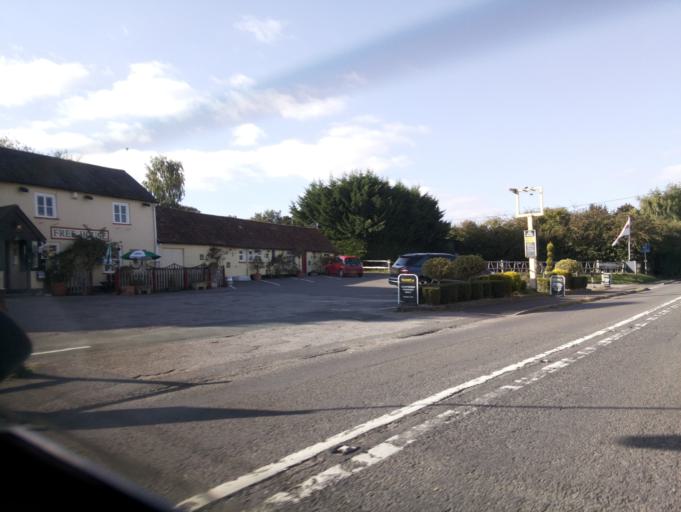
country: GB
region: England
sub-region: Hampshire
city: Alton
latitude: 51.1116
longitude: -0.9941
